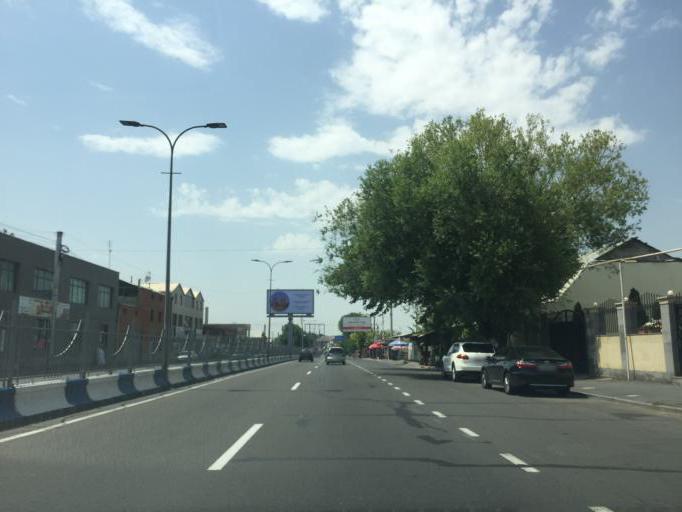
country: AM
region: Ararat
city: Argavand
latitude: 40.1608
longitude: 44.4254
